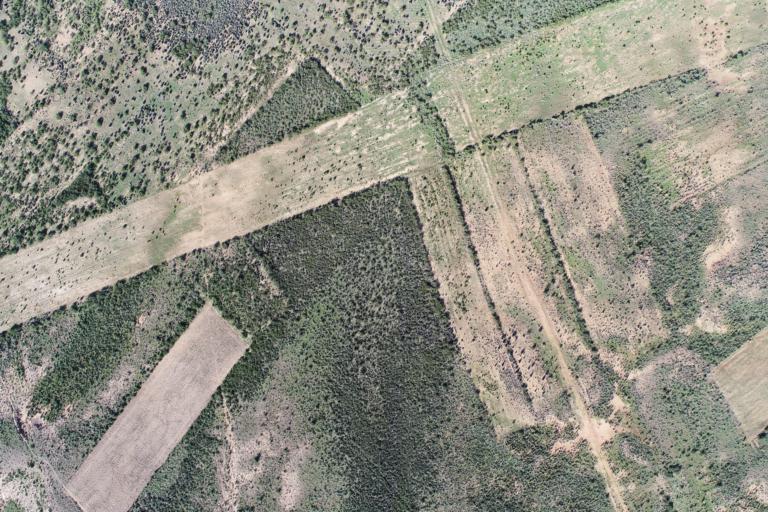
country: BO
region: La Paz
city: Curahuara de Carangas
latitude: -17.3004
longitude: -68.4978
